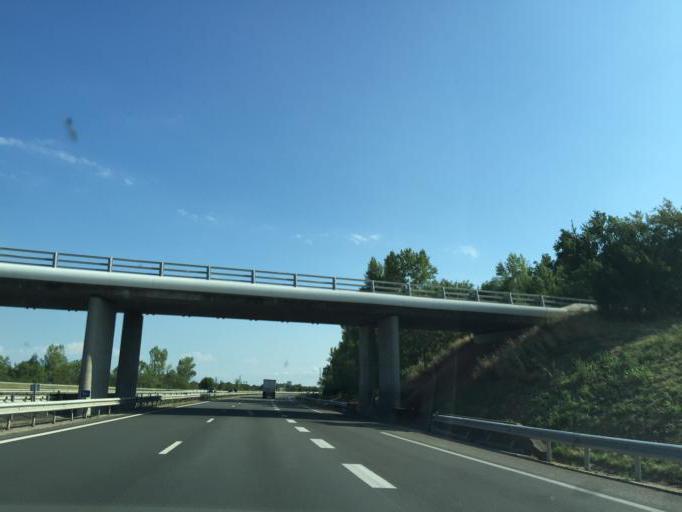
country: FR
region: Rhone-Alpes
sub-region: Departement de la Loire
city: Feurs
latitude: 45.7353
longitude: 4.1824
